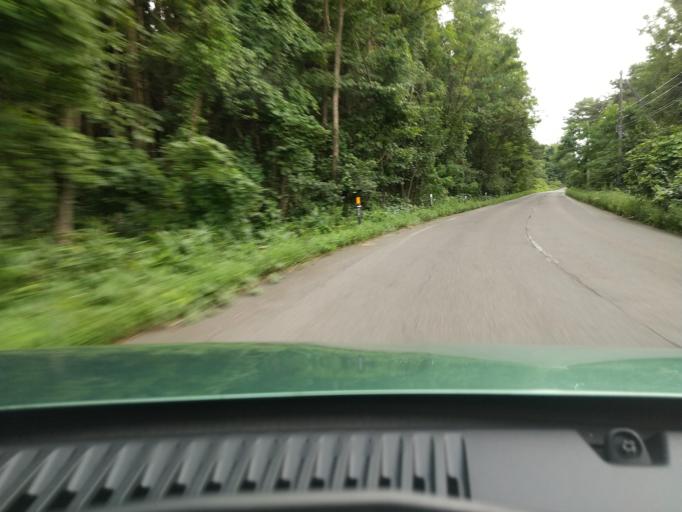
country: JP
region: Akita
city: Akita
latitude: 39.7686
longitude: 140.1347
